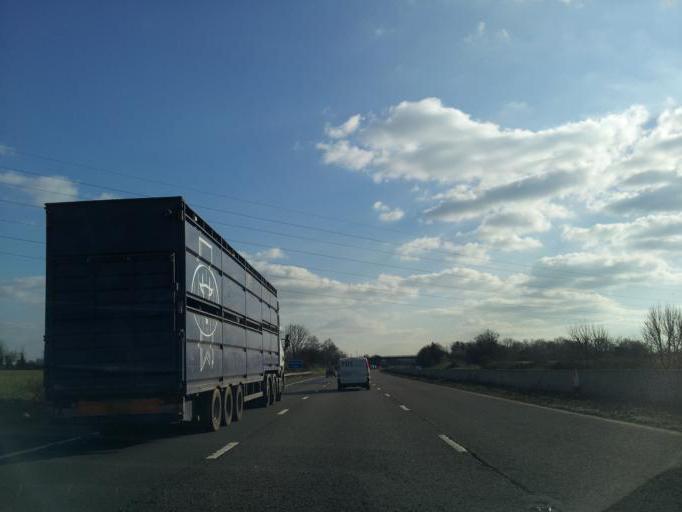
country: GB
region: England
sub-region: Somerset
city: North Petherton
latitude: 51.0859
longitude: -3.0053
